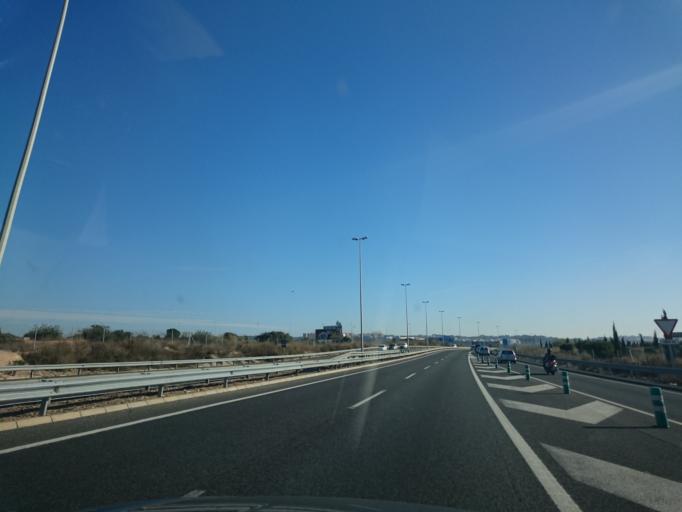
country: ES
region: Catalonia
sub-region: Provincia de Tarragona
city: Constanti
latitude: 41.1316
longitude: 1.2085
